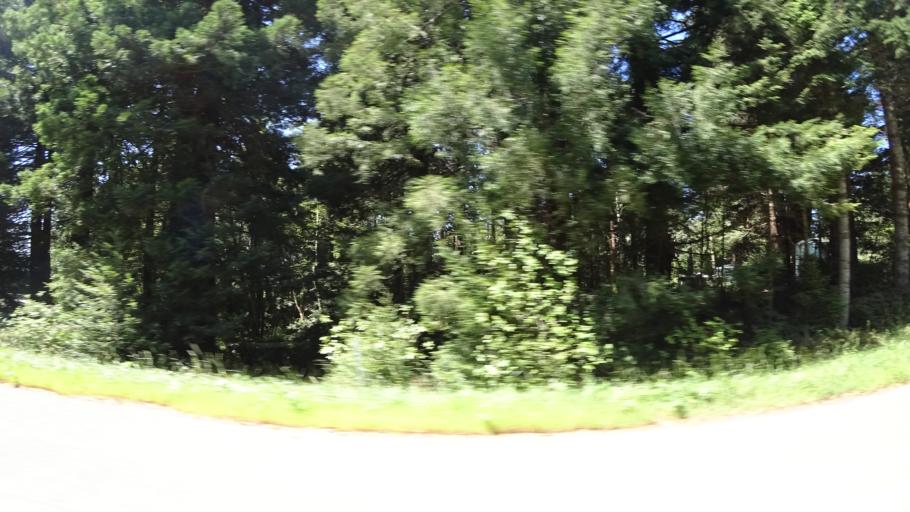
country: US
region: California
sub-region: Humboldt County
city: Westhaven-Moonstone
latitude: 41.0948
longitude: -124.1517
